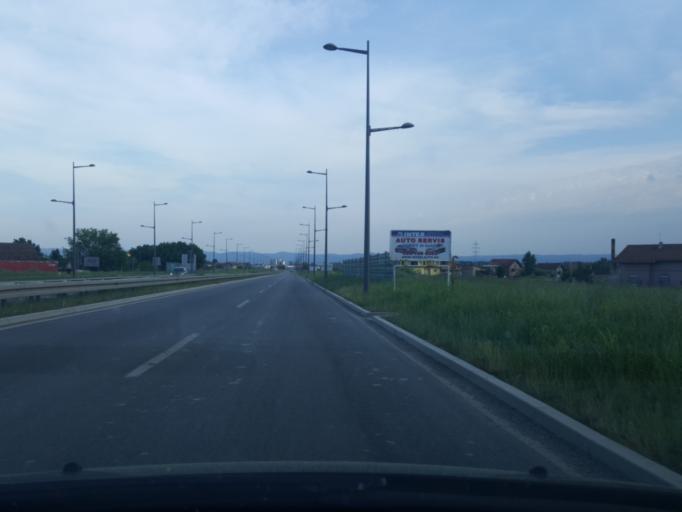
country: RS
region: Autonomna Pokrajina Vojvodina
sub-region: Juznobacki Okrug
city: Novi Sad
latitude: 45.3015
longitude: 19.8077
